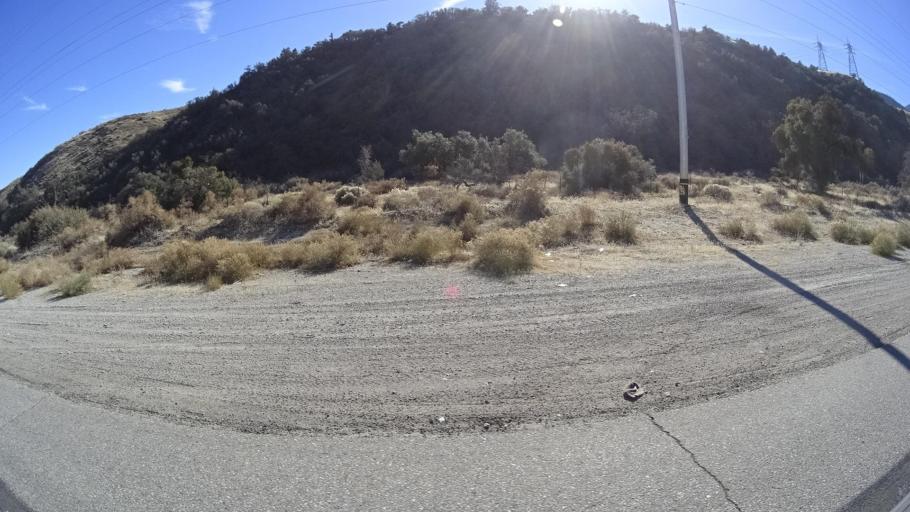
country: US
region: California
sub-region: Kern County
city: Frazier Park
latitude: 34.8182
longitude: -118.9034
